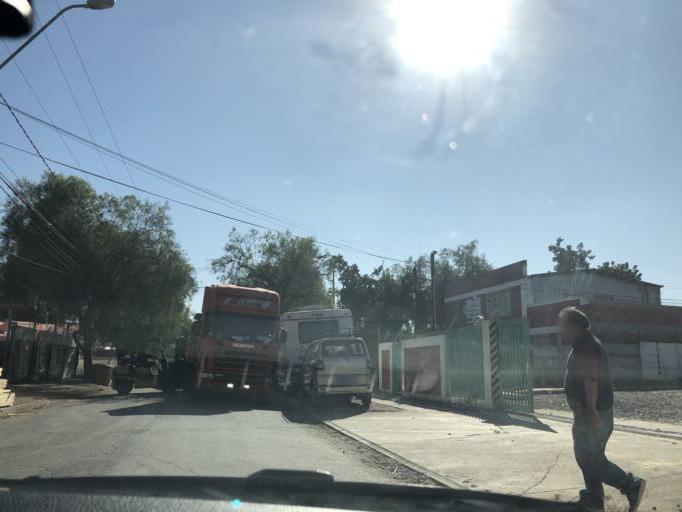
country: CL
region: Santiago Metropolitan
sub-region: Provincia de Cordillera
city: Puente Alto
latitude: -33.6174
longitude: -70.6111
